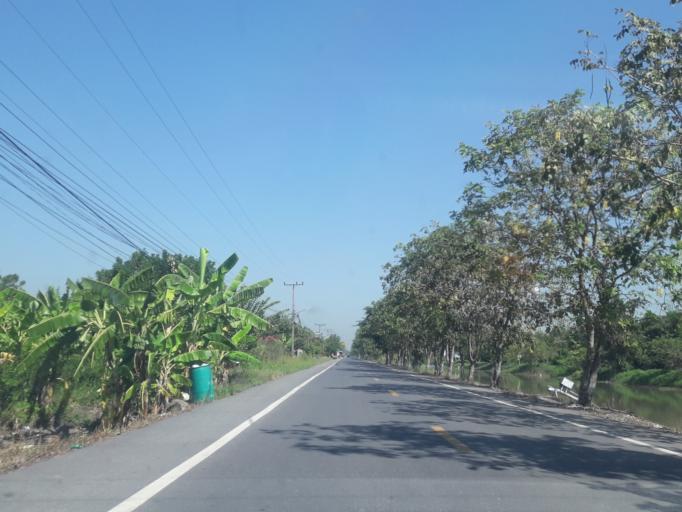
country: TH
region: Pathum Thani
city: Nong Suea
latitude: 14.1618
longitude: 100.8459
